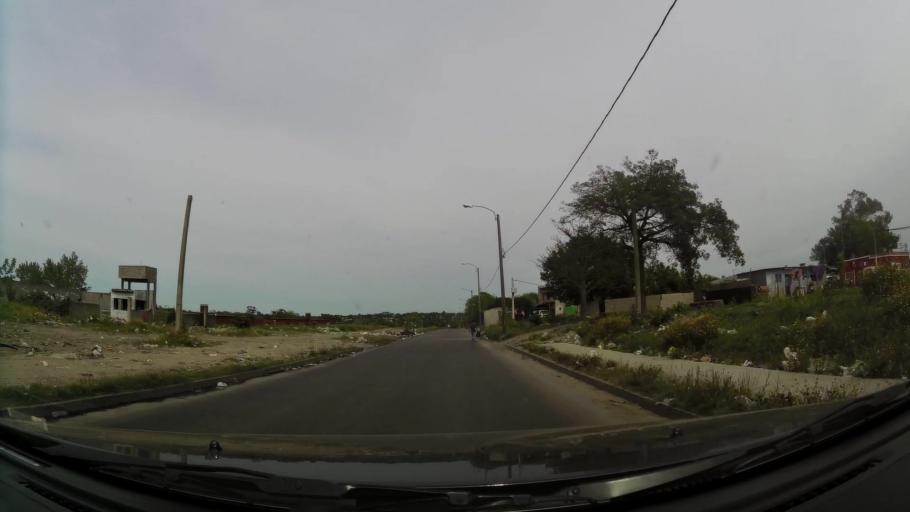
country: UY
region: Montevideo
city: Montevideo
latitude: -34.8362
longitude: -56.1746
